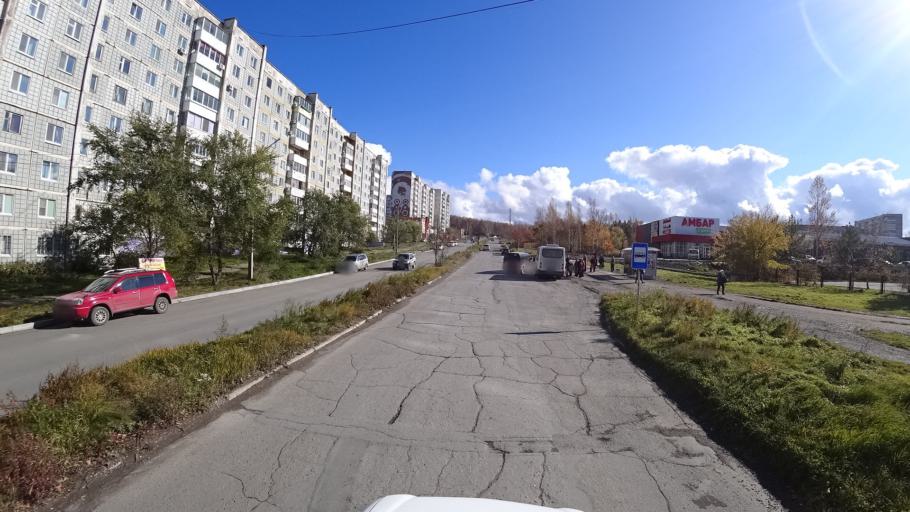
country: RU
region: Khabarovsk Krai
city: Amursk
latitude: 50.2434
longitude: 136.9155
